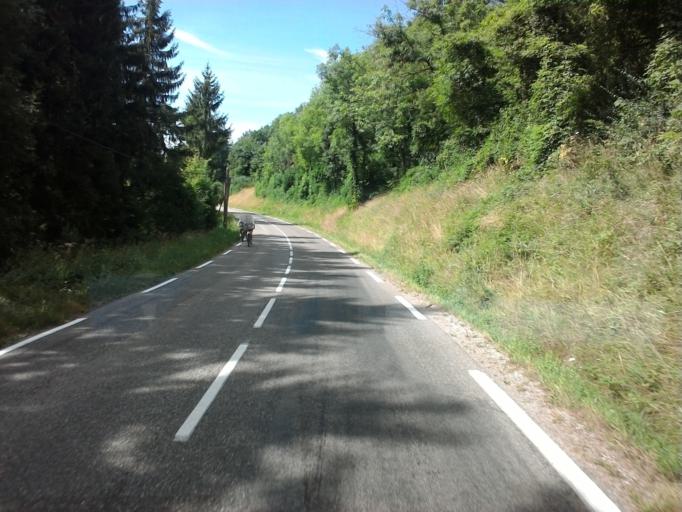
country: FR
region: Rhone-Alpes
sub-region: Departement de l'Isere
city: Bilieu
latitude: 45.4640
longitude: 5.5378
